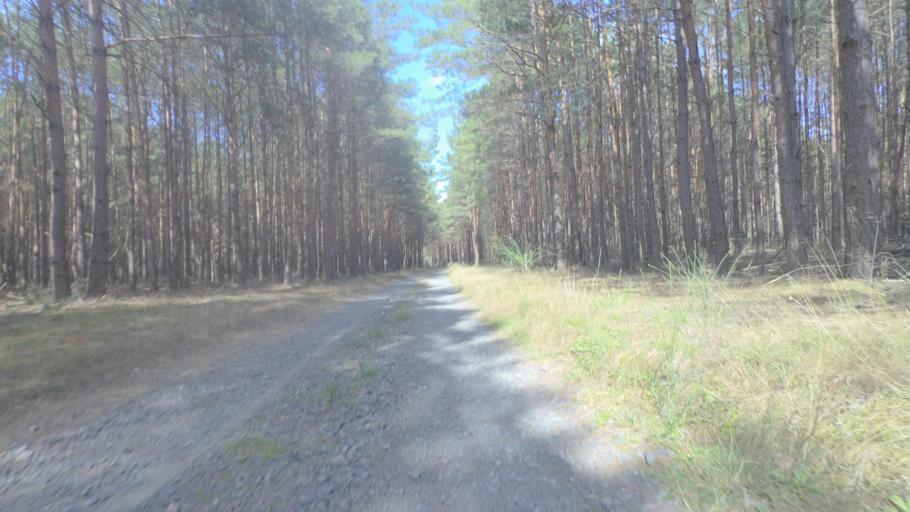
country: DE
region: Brandenburg
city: Munchehofe
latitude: 52.1778
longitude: 13.8721
